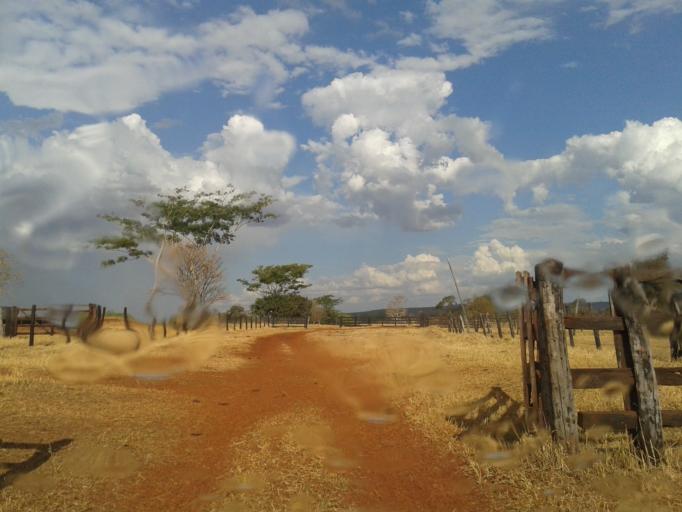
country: BR
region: Minas Gerais
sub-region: Santa Vitoria
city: Santa Vitoria
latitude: -19.1709
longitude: -49.9941
